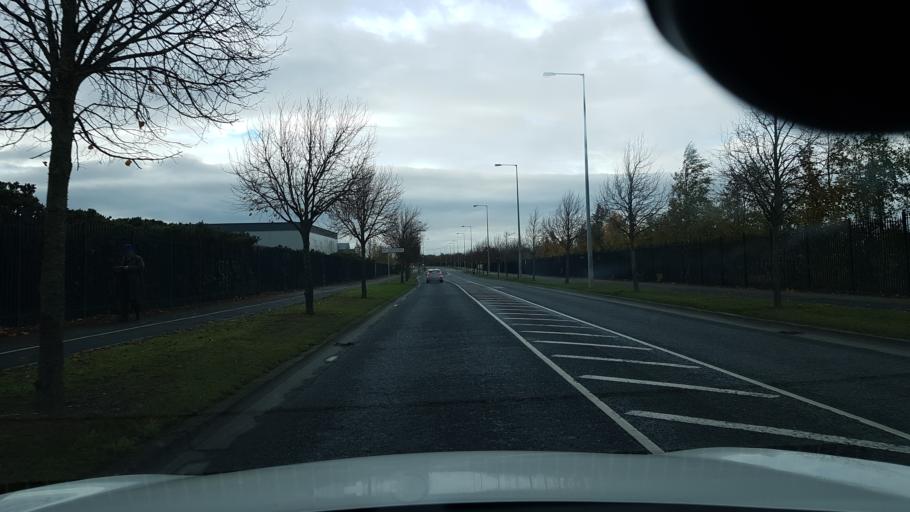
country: IE
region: Leinster
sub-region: Fingal County
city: Blanchardstown
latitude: 53.4101
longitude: -6.3734
